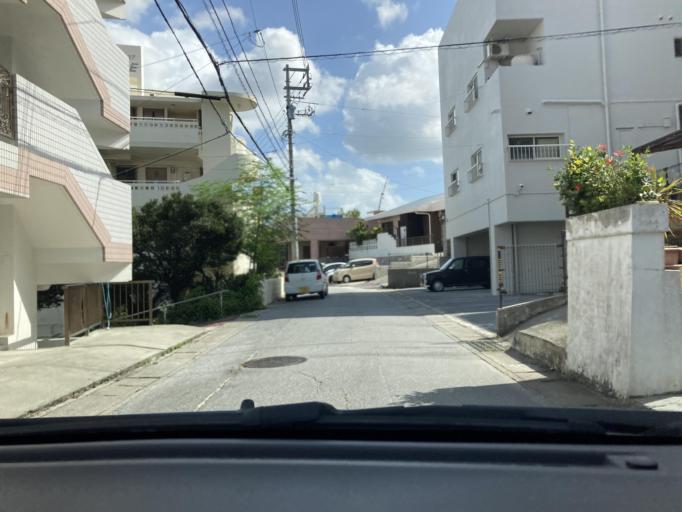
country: JP
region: Okinawa
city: Tomigusuku
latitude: 26.1975
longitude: 127.6749
